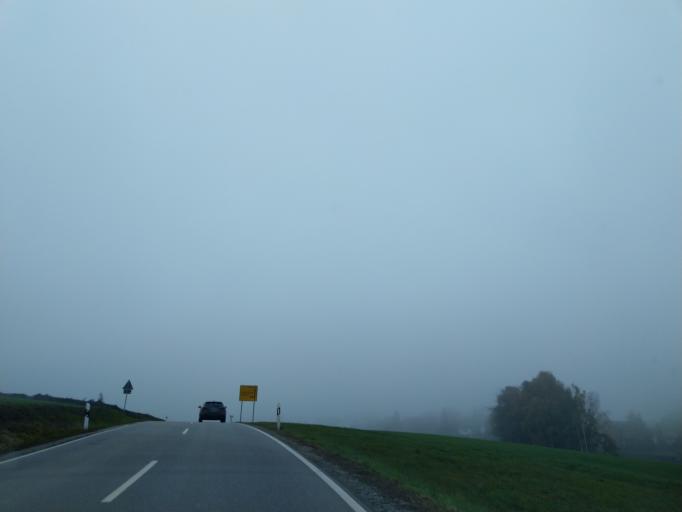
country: DE
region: Bavaria
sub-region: Lower Bavaria
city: Schollnach
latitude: 48.7709
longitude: 13.1856
